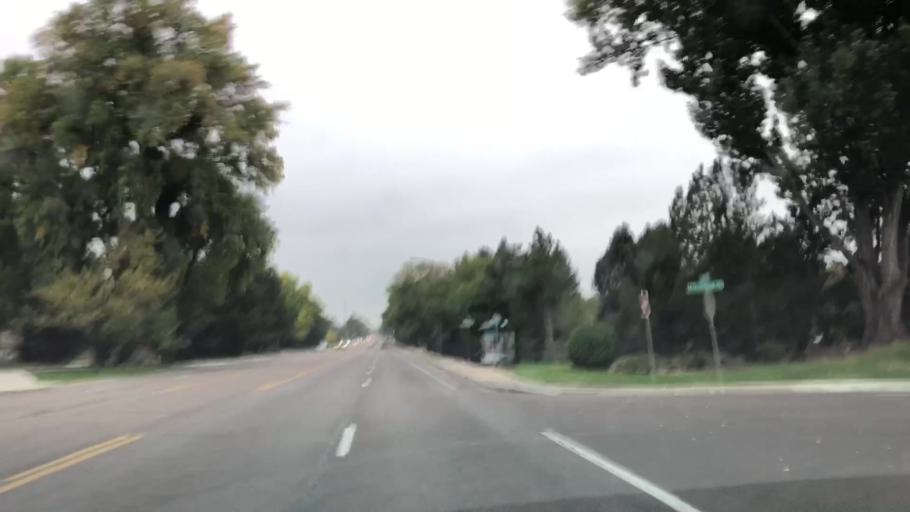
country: US
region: Colorado
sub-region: Larimer County
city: Fort Collins
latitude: 40.5566
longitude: -105.0581
